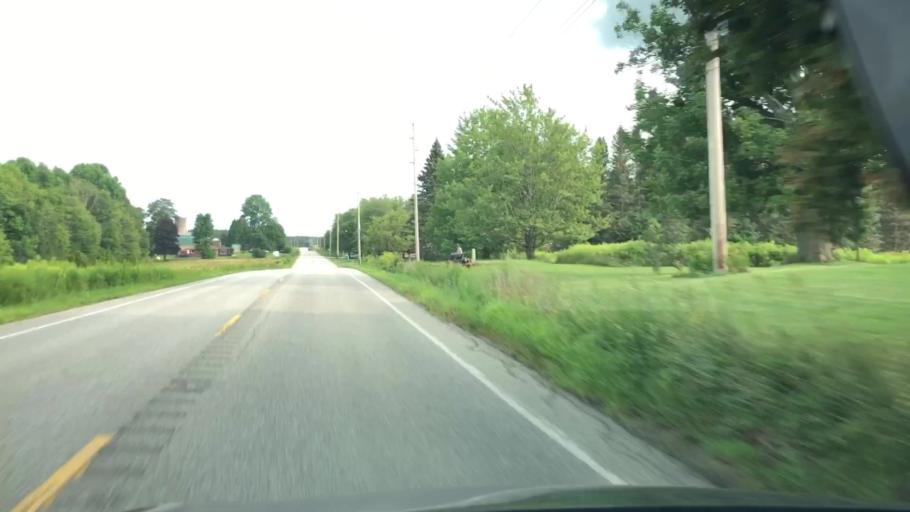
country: US
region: Pennsylvania
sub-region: Erie County
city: Union City
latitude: 41.9524
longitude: -79.8507
